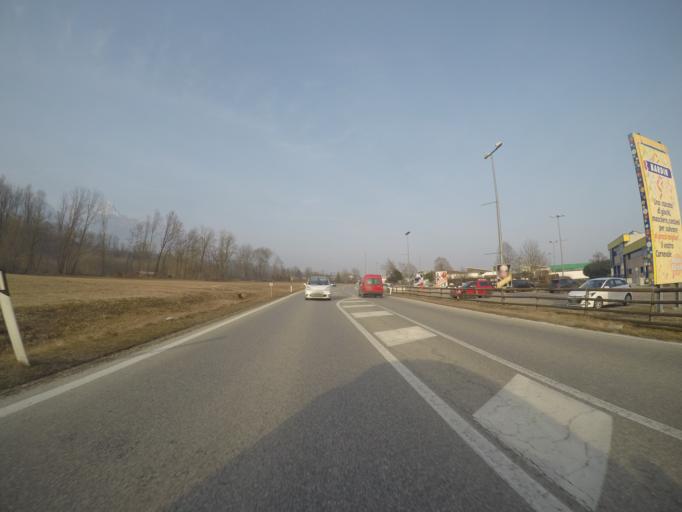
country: IT
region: Veneto
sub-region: Provincia di Belluno
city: Santa Giustina
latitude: 46.0721
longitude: 12.0186
